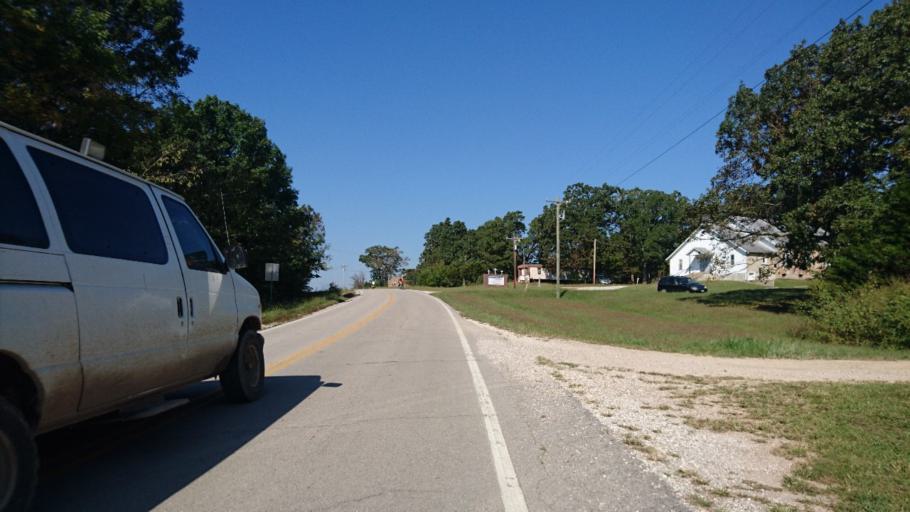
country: US
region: Missouri
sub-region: Pulaski County
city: Richland
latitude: 37.7670
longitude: -92.4023
